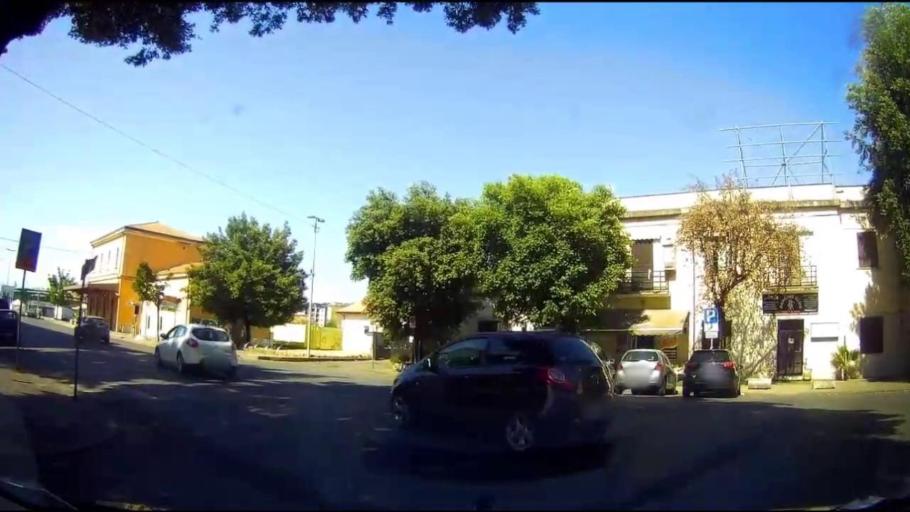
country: IT
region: Calabria
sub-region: Provincia di Cosenza
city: Cosenza
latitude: 39.2937
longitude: 16.2566
